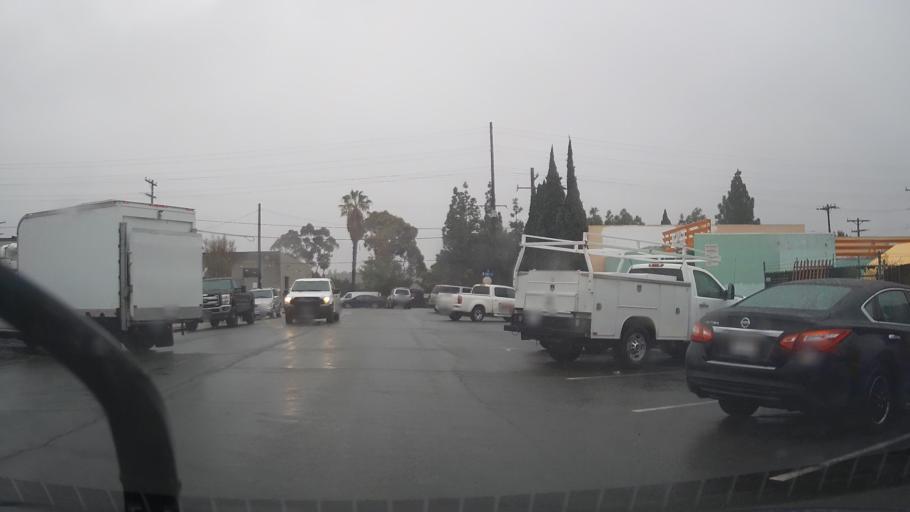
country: US
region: California
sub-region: San Diego County
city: San Diego
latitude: 32.7138
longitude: -117.1241
